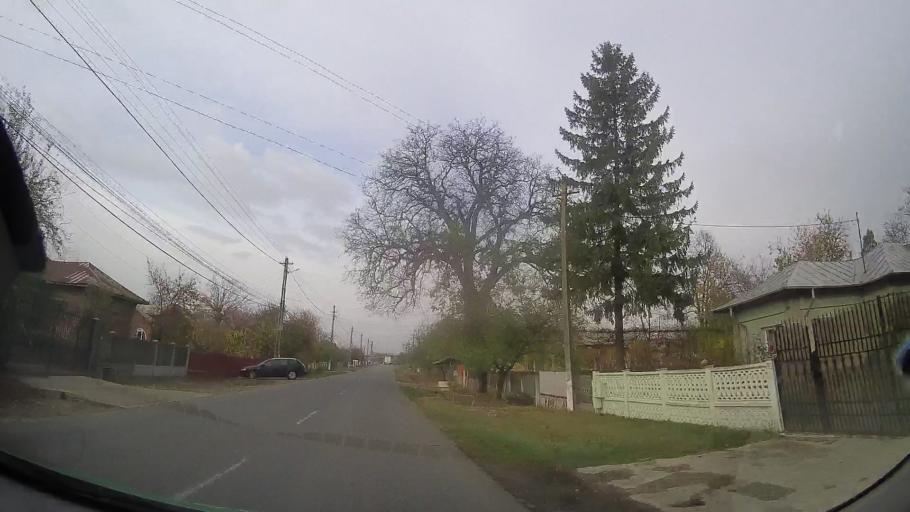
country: RO
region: Prahova
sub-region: Comuna Gorgota
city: Potigrafu
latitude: 44.7796
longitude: 26.1032
